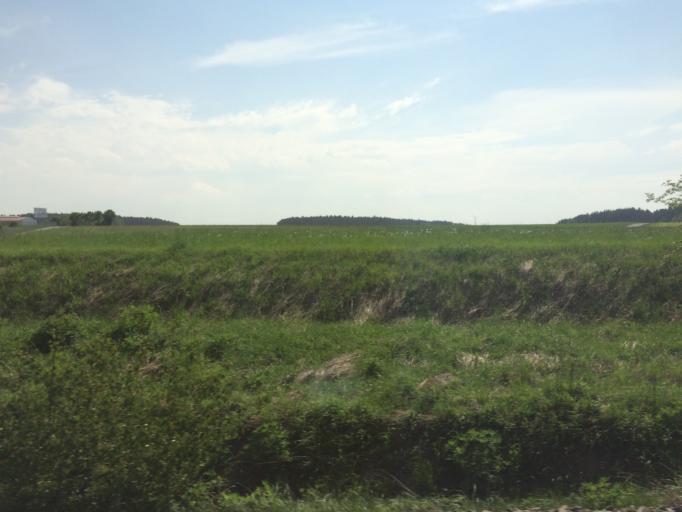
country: DE
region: Bavaria
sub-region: Regierungsbezirk Mittelfranken
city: Emskirchen
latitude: 49.5624
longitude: 10.6895
